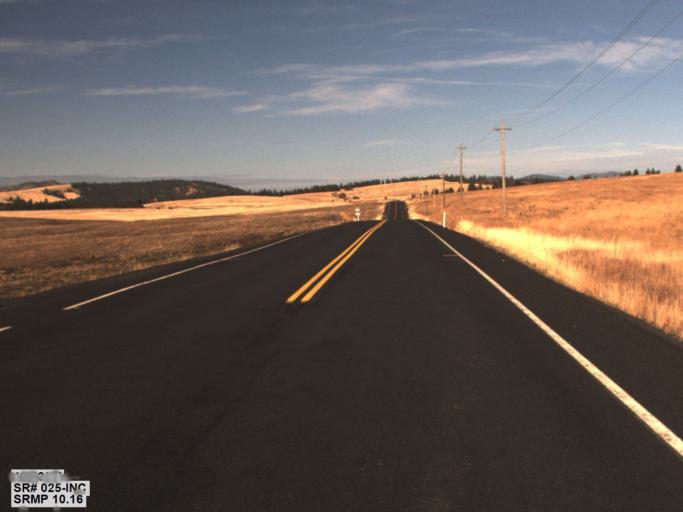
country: US
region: Washington
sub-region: Lincoln County
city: Davenport
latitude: 47.7956
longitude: -118.1737
